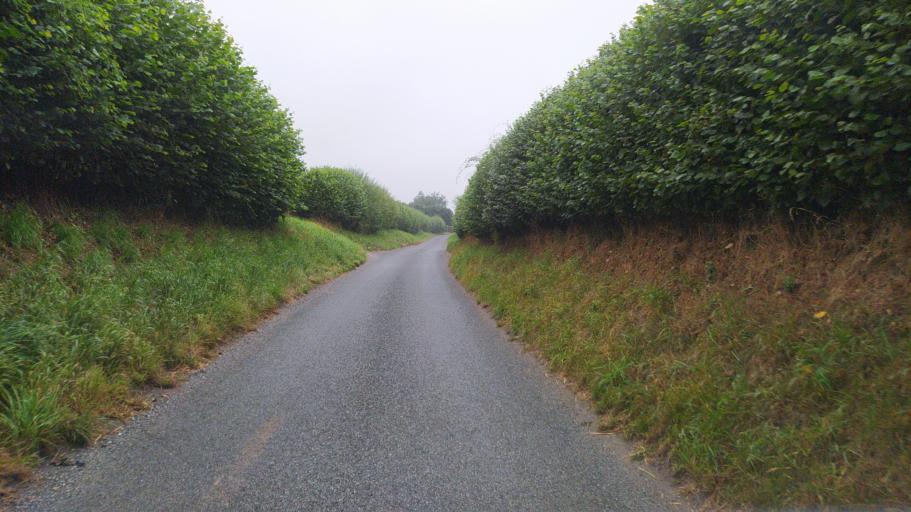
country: GB
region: England
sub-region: Wiltshire
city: Ansty
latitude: 51.0087
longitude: -2.1109
